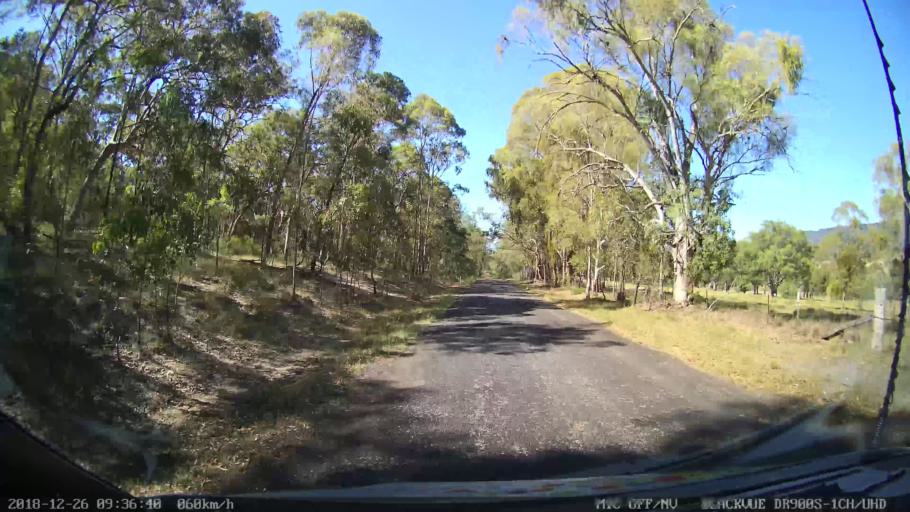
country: AU
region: New South Wales
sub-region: Mid-Western Regional
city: Kandos
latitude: -32.9259
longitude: 150.0399
